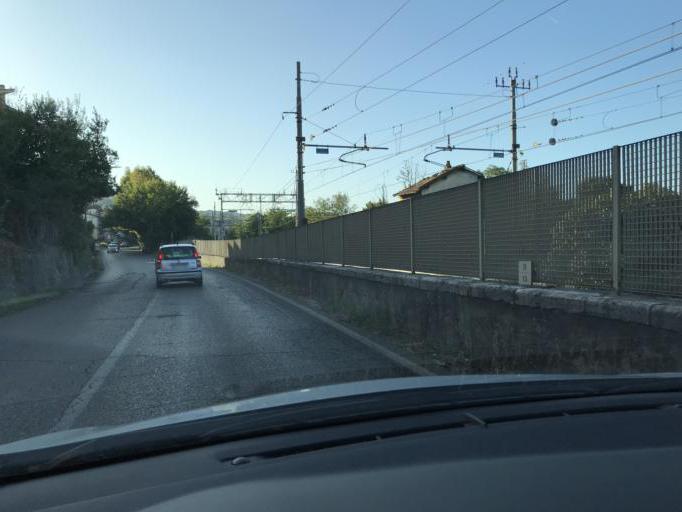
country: IT
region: Latium
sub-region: Provincia di Viterbo
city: Orte Scalo
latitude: 42.4436
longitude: 12.4032
